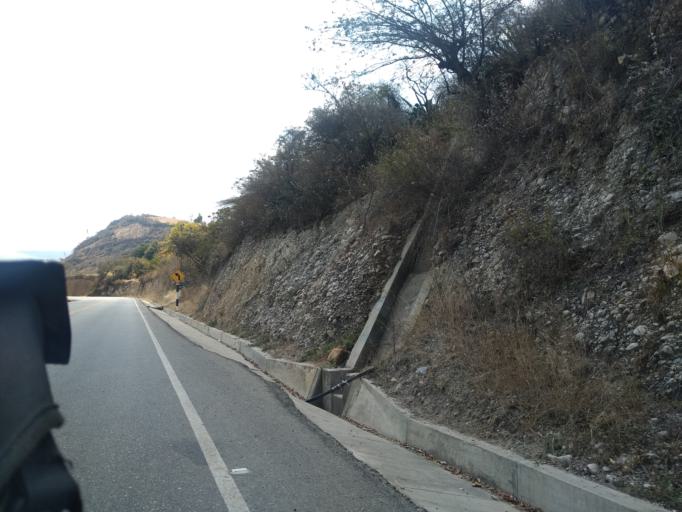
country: PE
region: Cajamarca
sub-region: Provincia de Cajabamba
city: Cauday
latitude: -7.6126
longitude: -78.0852
